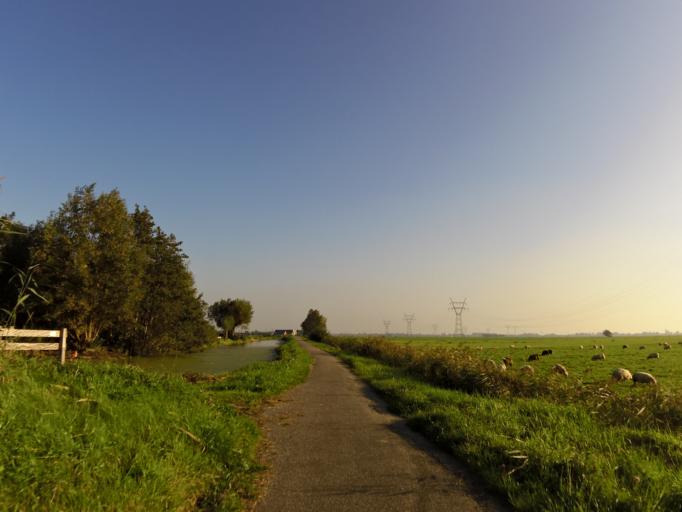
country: NL
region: South Holland
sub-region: Gemeente Leiderdorp
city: Leiderdorp
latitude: 52.1586
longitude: 4.5642
